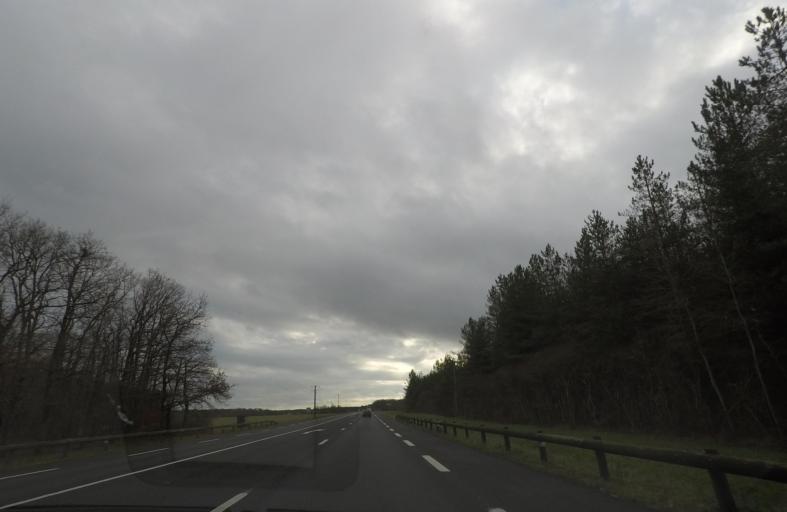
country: FR
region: Centre
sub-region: Departement du Loir-et-Cher
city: Soings-en-Sologne
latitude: 47.4497
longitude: 1.5355
